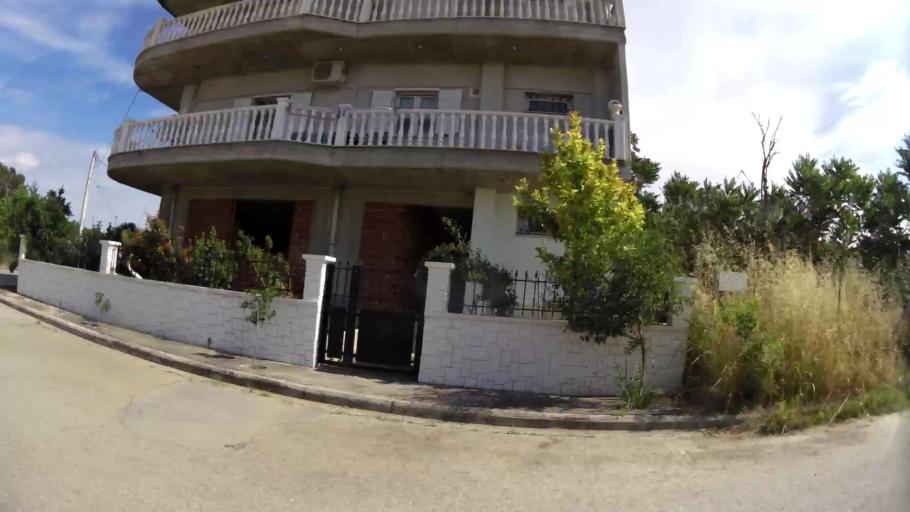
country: GR
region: Central Macedonia
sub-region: Nomos Pierias
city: Katerini
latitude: 40.2735
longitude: 22.4850
